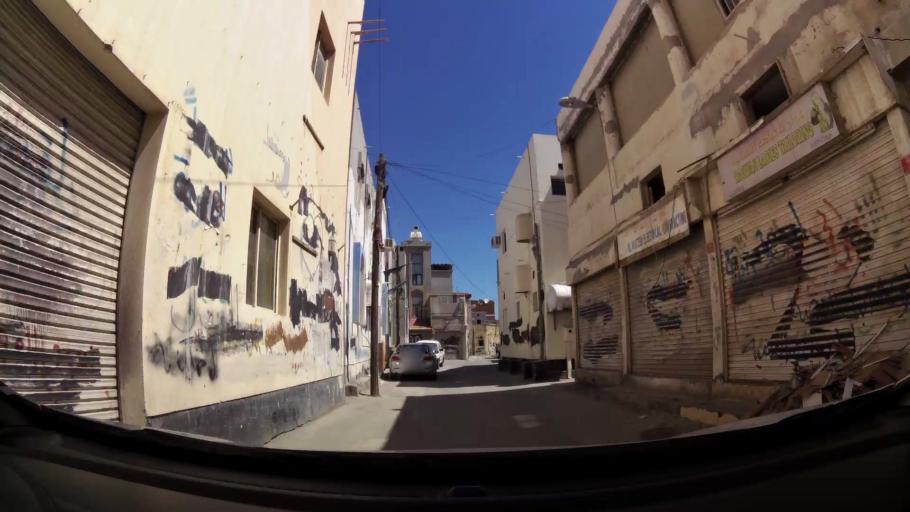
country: BH
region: Muharraq
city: Al Muharraq
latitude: 26.2852
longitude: 50.6249
